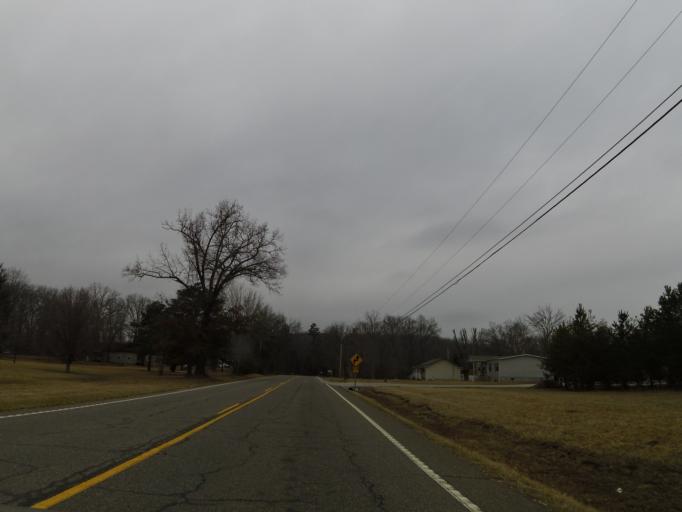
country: US
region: Tennessee
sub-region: Morgan County
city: Wartburg
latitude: 36.2664
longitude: -84.6607
